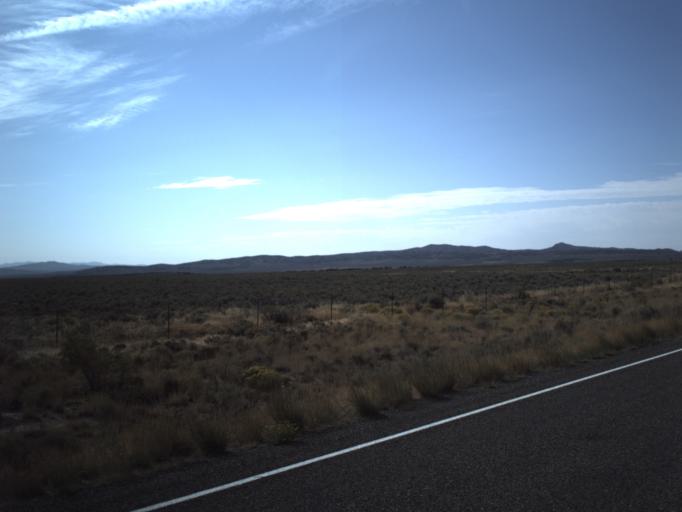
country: US
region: Idaho
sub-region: Cassia County
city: Burley
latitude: 41.7487
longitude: -113.5166
